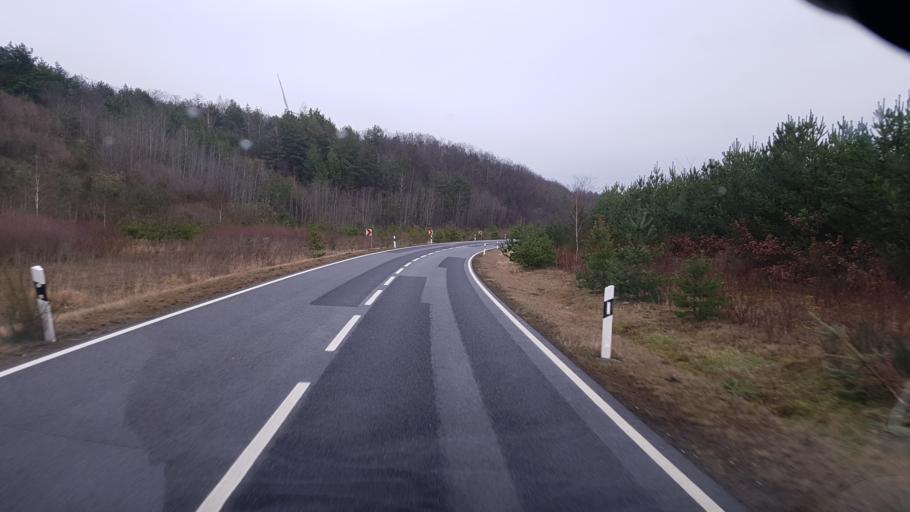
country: DE
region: Brandenburg
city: Schipkau
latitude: 51.5056
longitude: 13.8663
